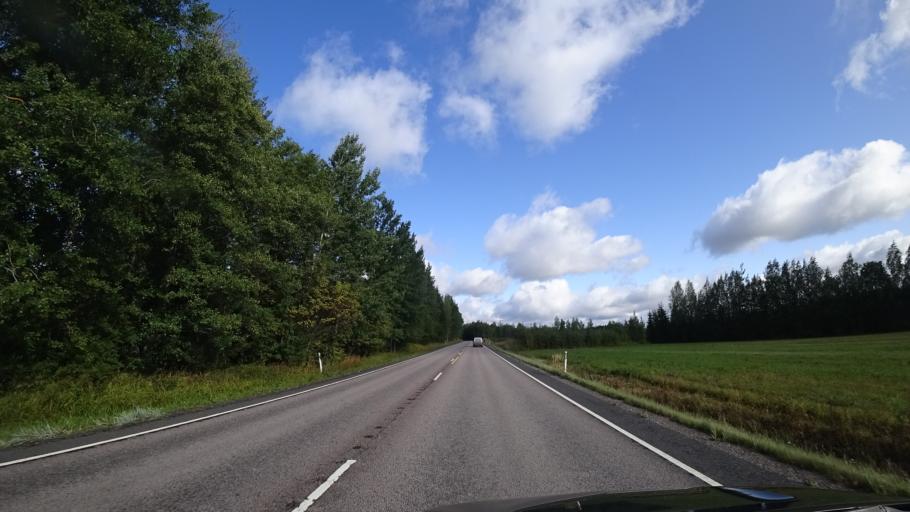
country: FI
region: Uusimaa
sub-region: Helsinki
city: Tuusula
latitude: 60.4897
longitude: 24.9390
